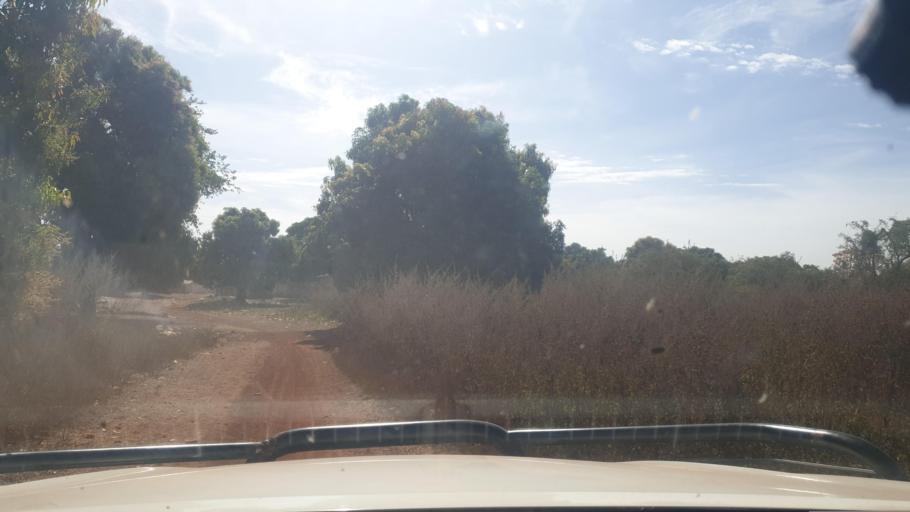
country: GN
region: Kankan
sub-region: Mandiana Prefecture
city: Mandiana
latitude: 10.4912
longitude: -8.0998
